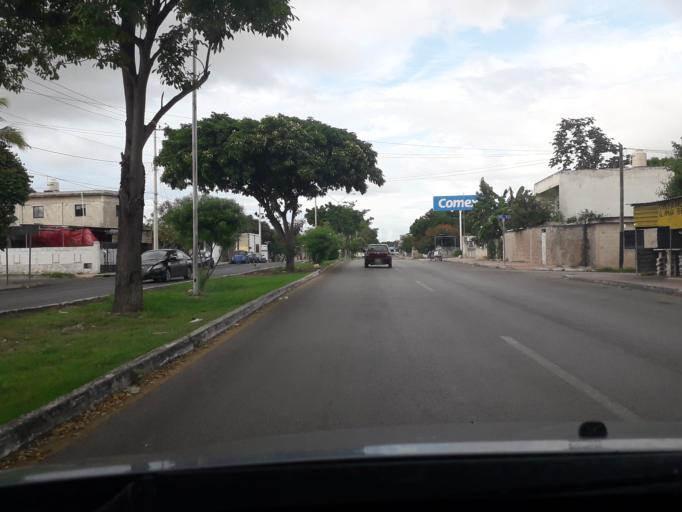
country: MX
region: Yucatan
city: Merida
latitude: 20.9650
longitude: -89.6636
